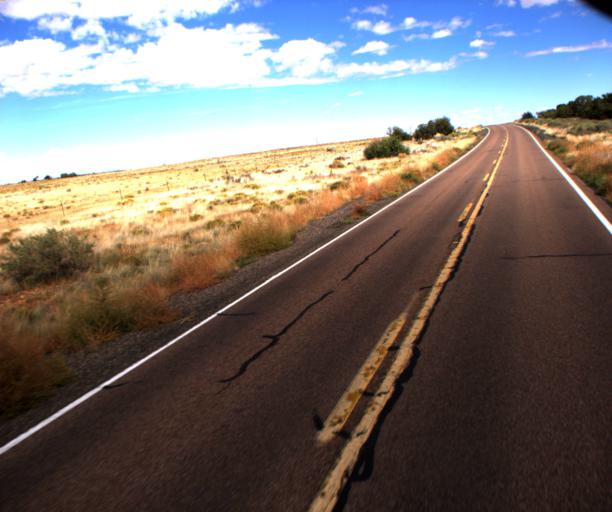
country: US
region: Arizona
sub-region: Navajo County
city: Snowflake
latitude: 34.6628
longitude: -110.3277
